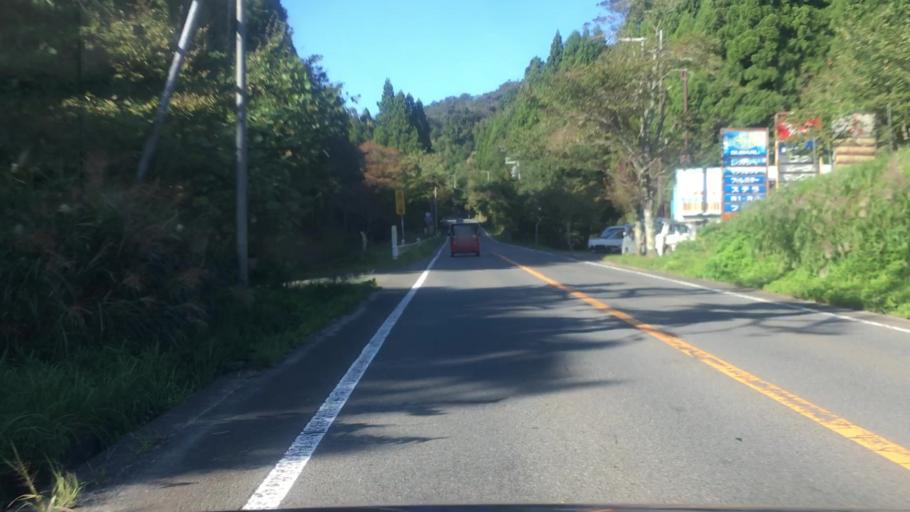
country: JP
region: Hyogo
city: Toyooka
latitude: 35.5637
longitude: 134.8523
